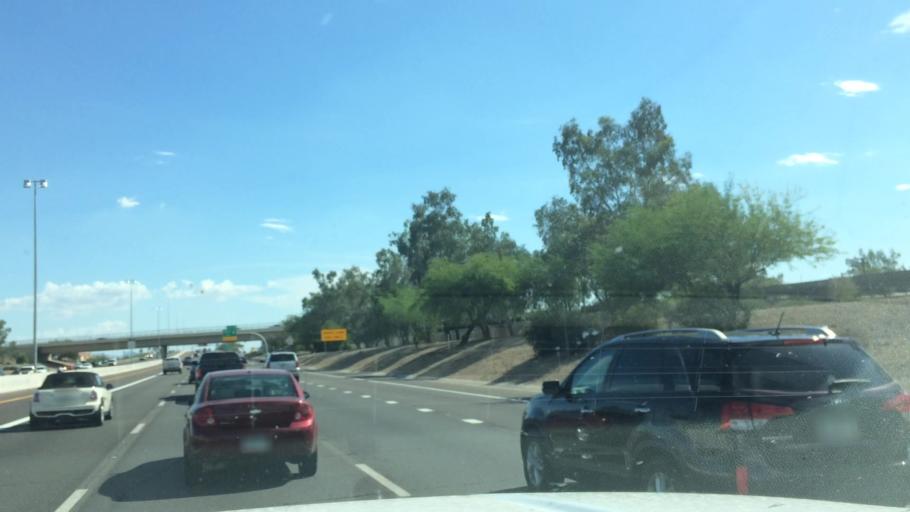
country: US
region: Arizona
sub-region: Maricopa County
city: Sun City
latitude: 33.6458
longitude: -112.2339
